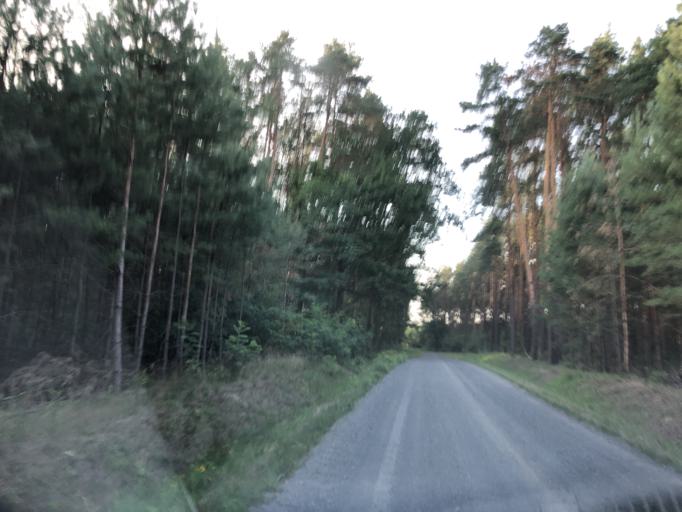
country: PL
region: Lubusz
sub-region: Powiat swiebodzinski
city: Zbaszynek
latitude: 52.2331
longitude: 15.7916
